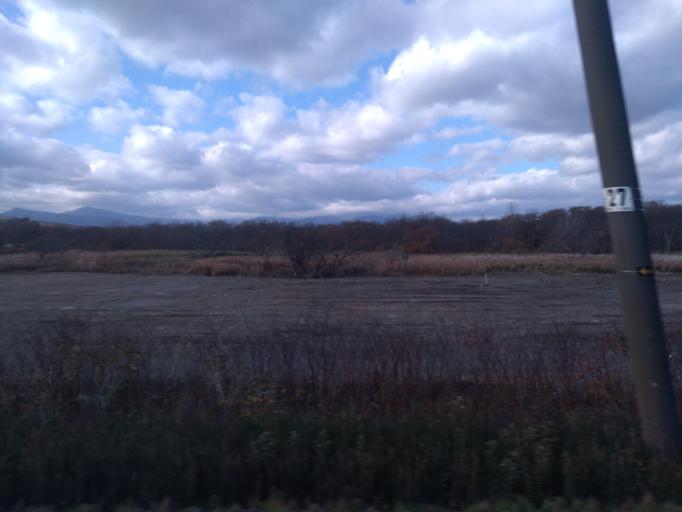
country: JP
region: Hokkaido
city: Shiraoi
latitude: 42.5034
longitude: 141.2772
